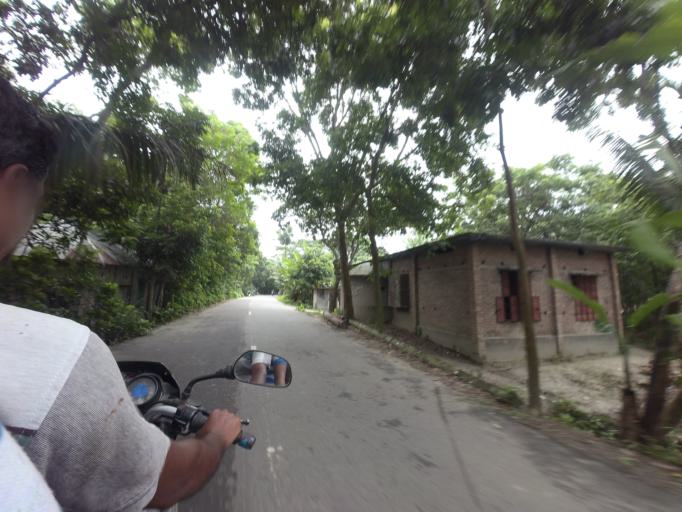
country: BD
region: Khulna
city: Kalia
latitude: 23.1530
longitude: 89.6446
